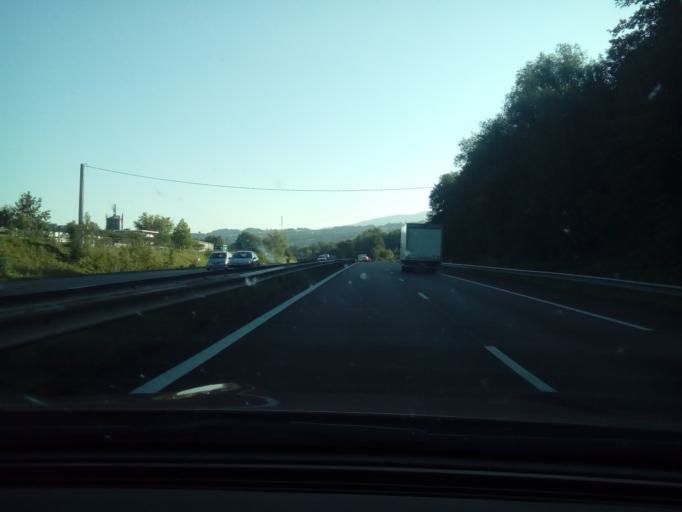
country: FR
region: Rhone-Alpes
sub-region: Departement de la Savoie
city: La Biolle
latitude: 45.7483
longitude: 5.9344
